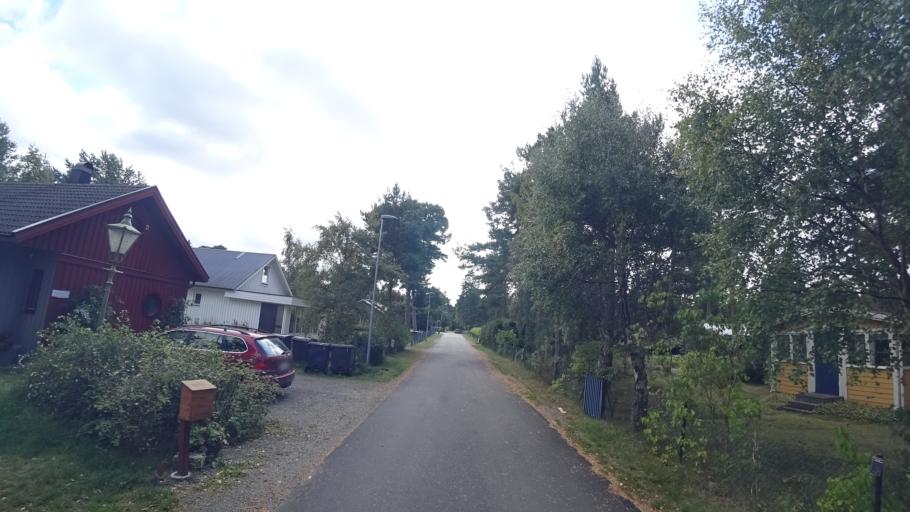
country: SE
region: Skane
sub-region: Kristianstads Kommun
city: Ahus
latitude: 55.9365
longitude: 14.3123
